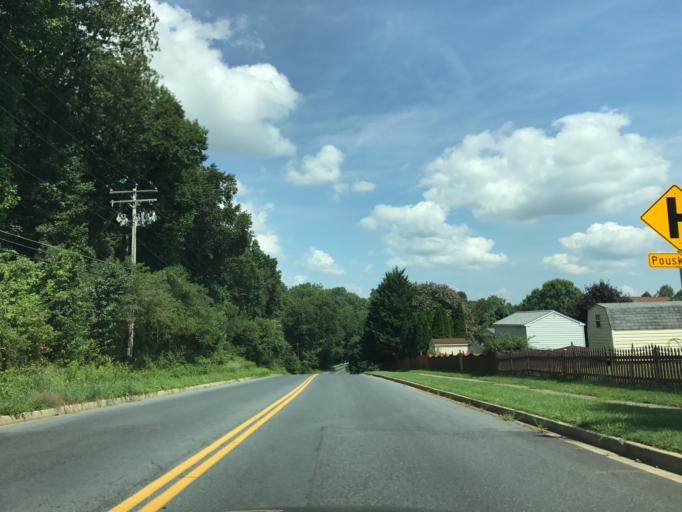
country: US
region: Maryland
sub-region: Harford County
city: Riverside
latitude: 39.4787
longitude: -76.2835
